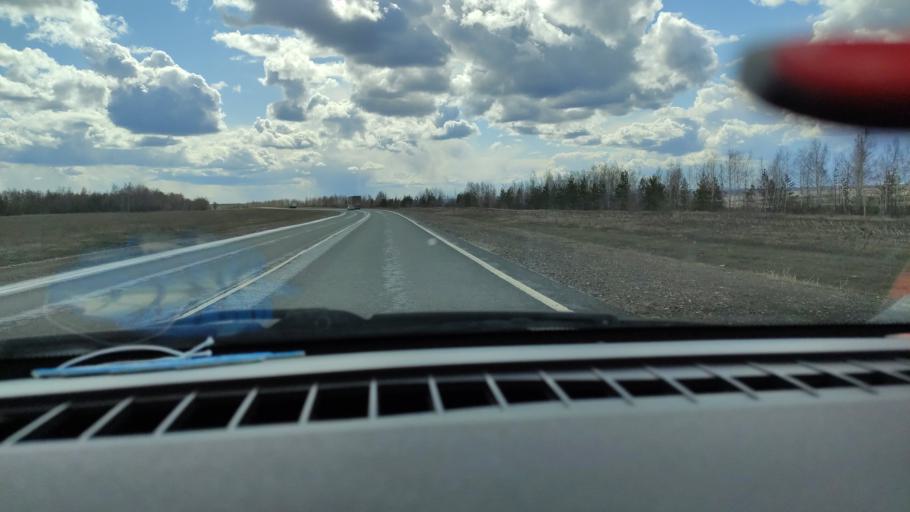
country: RU
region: Samara
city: Syzran'
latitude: 52.8597
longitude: 48.2634
